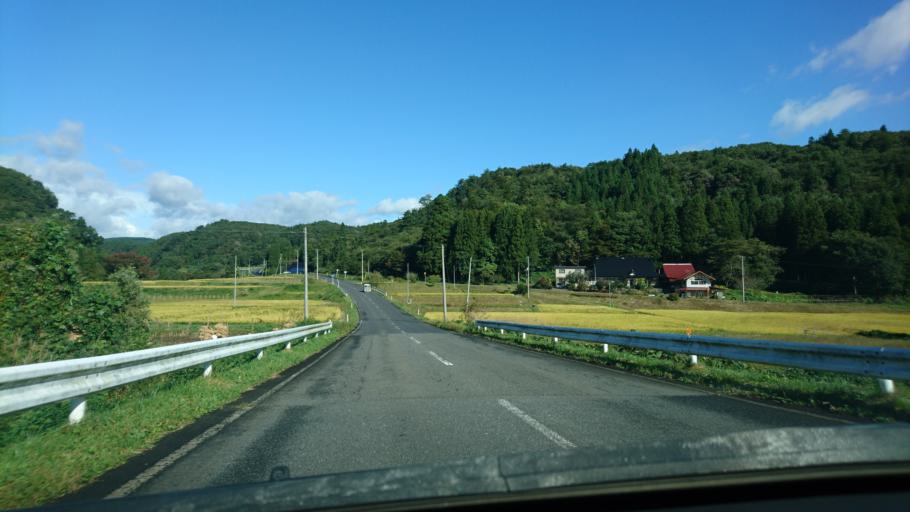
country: JP
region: Iwate
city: Ichinoseki
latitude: 39.0192
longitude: 141.0230
